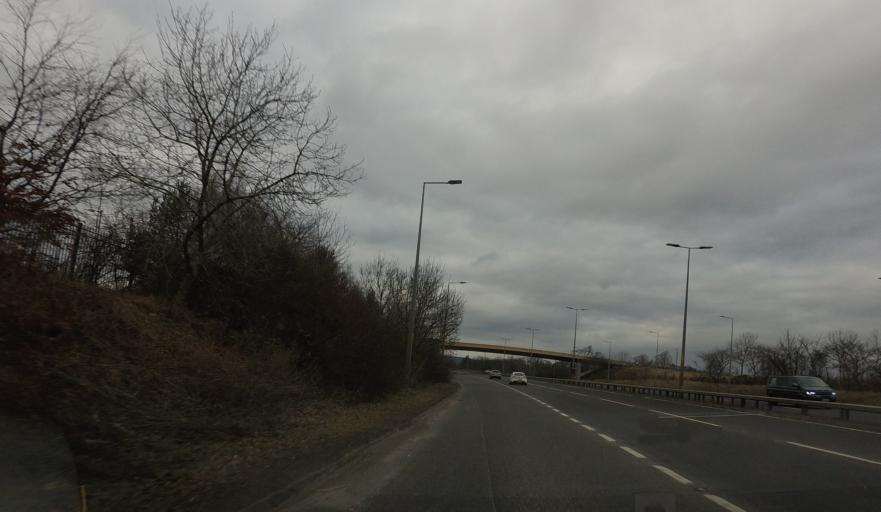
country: GB
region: Scotland
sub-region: Highland
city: Inverness
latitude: 57.4783
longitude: -4.1888
